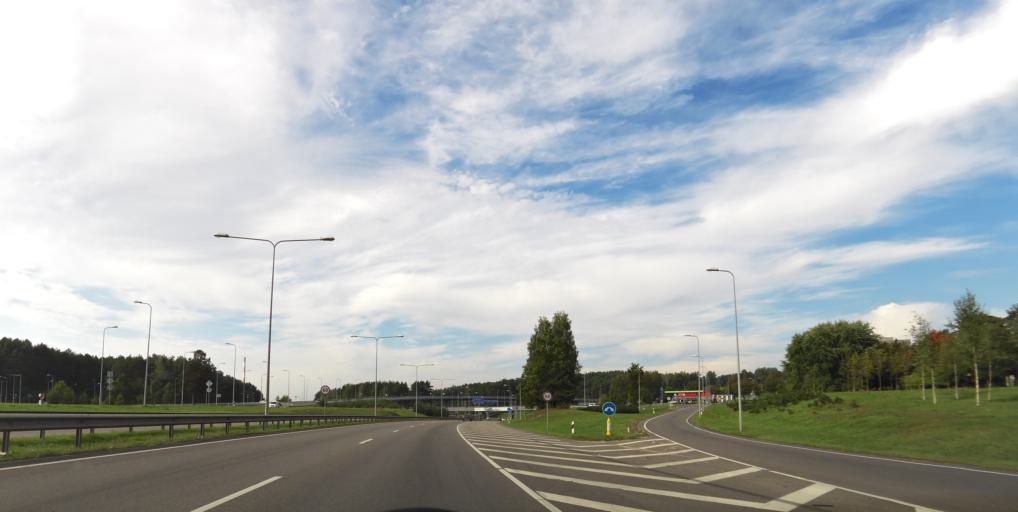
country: LT
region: Vilnius County
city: Lazdynai
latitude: 54.6708
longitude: 25.2019
